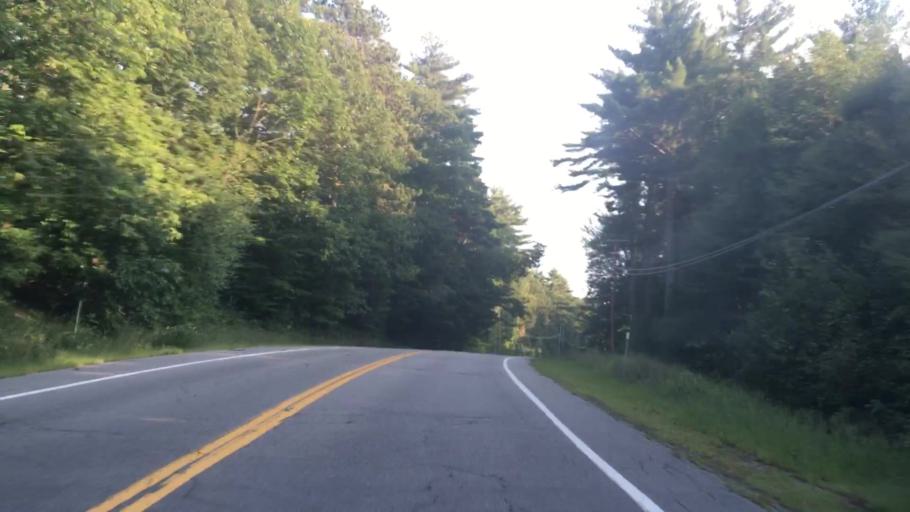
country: US
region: New Hampshire
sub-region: Belknap County
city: Gilmanton
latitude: 43.4550
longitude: -71.4215
